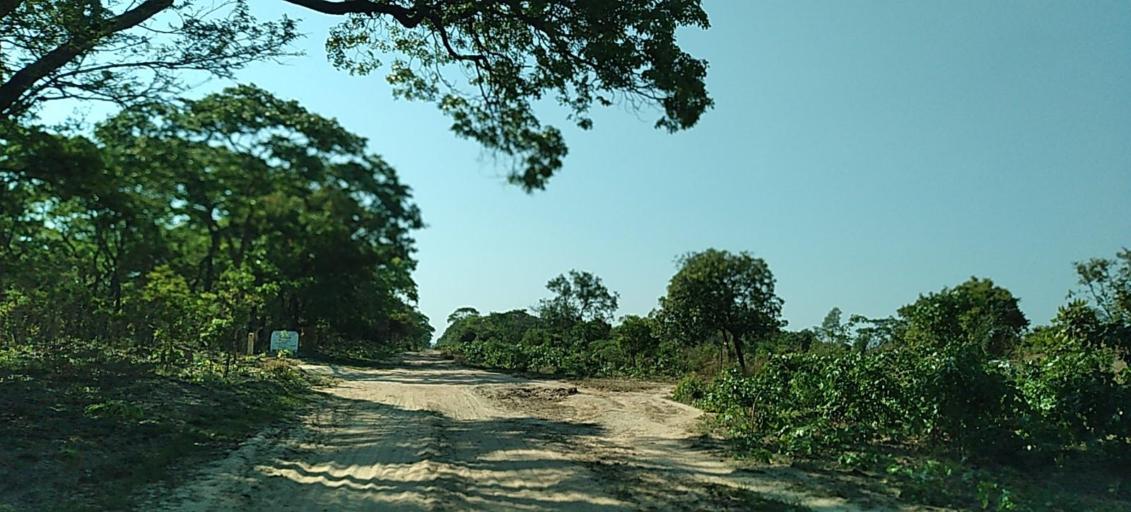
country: ZM
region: Central
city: Mkushi
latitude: -13.4770
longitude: 28.9218
